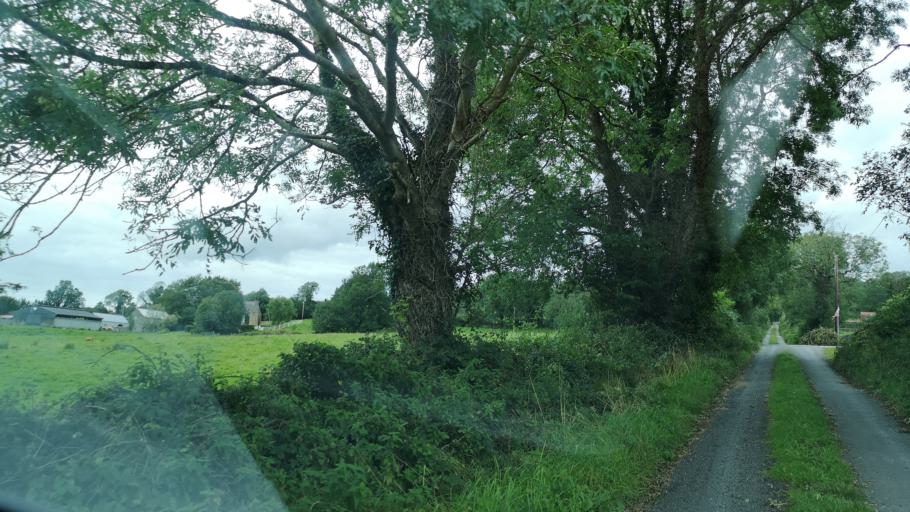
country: IE
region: Connaught
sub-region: County Galway
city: Loughrea
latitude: 53.1557
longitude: -8.4400
